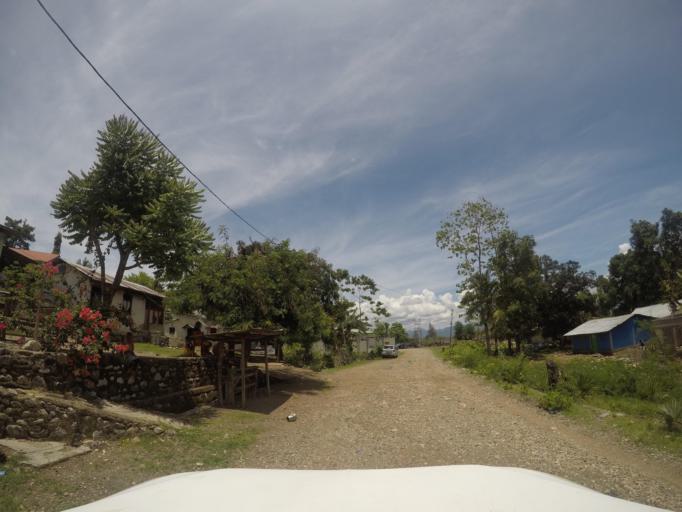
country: TL
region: Bobonaro
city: Maliana
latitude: -8.9959
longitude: 125.2187
